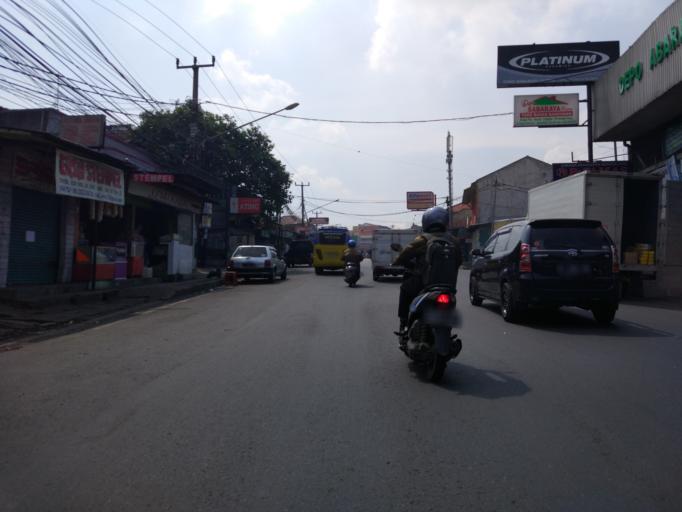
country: ID
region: West Java
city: Cileunyi
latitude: -6.9386
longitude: 107.7536
